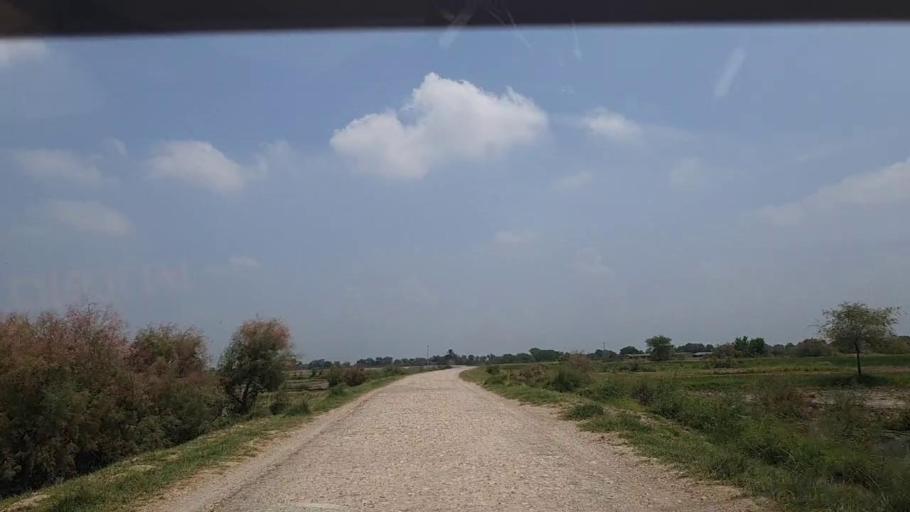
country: PK
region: Sindh
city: Khanpur
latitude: 27.8941
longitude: 69.3977
